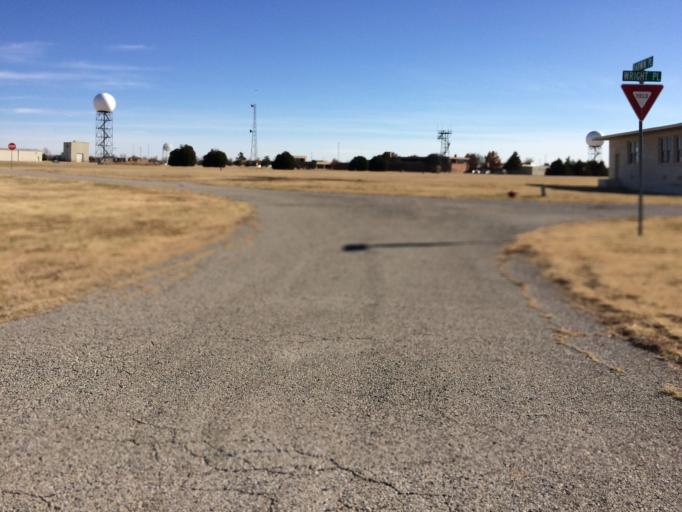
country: US
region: Oklahoma
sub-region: Cleveland County
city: Norman
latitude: 35.2398
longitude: -97.4640
